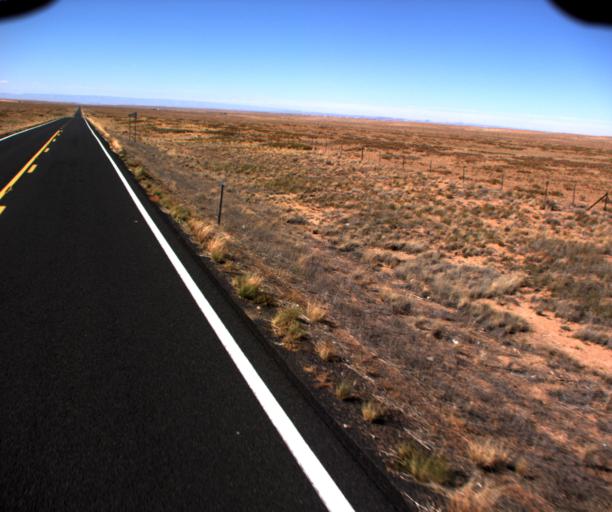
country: US
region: Arizona
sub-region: Coconino County
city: Tuba City
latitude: 36.0122
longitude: -111.0772
